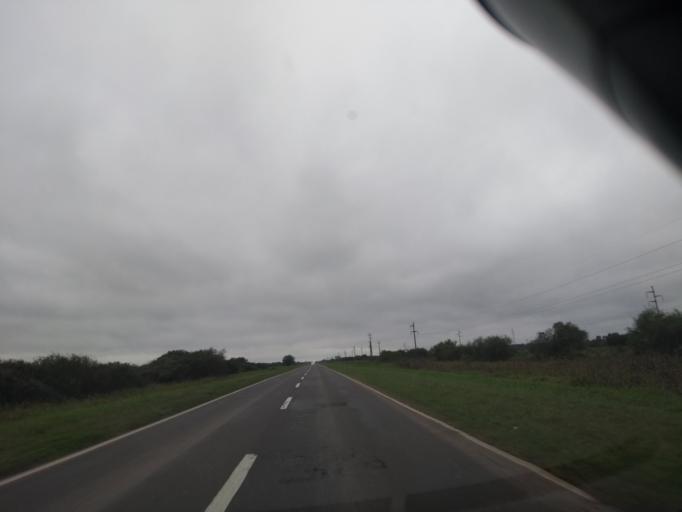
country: AR
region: Chaco
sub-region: Departamento de Quitilipi
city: Quitilipi
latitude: -26.8612
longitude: -60.2808
